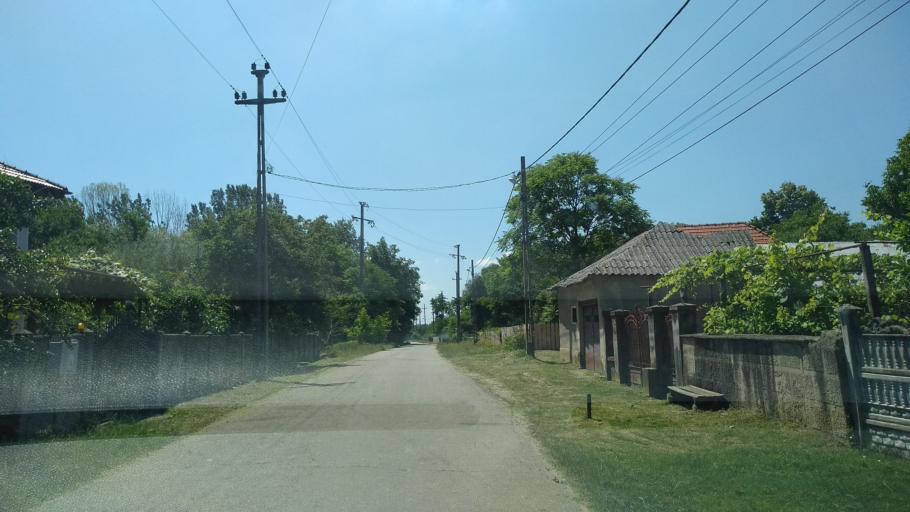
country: RO
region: Gorj
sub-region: Comuna Turcinesti
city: Turcinesti
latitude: 45.1129
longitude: 23.3164
